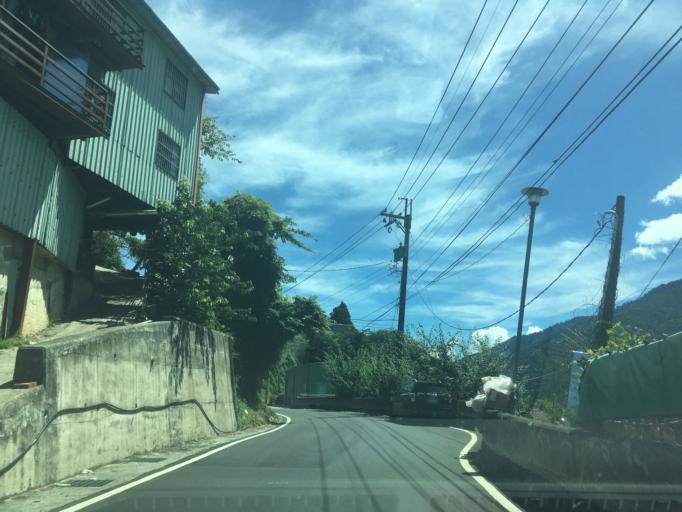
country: TW
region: Taiwan
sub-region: Nantou
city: Puli
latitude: 24.2551
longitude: 121.2613
